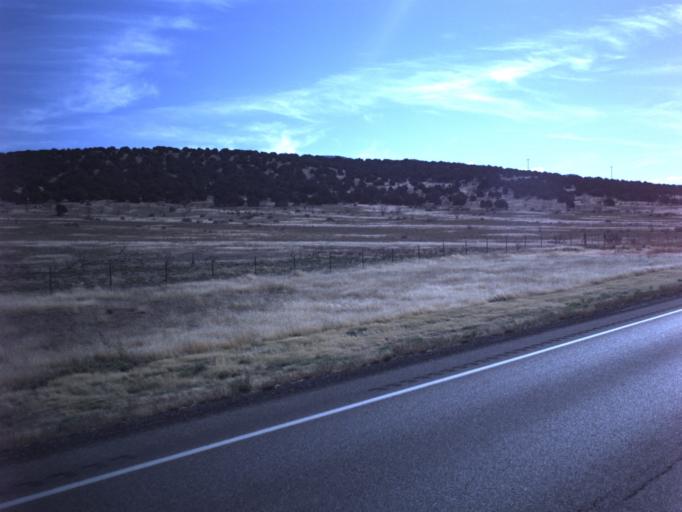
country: US
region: Utah
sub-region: Sanpete County
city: Gunnison
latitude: 39.3315
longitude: -111.9152
